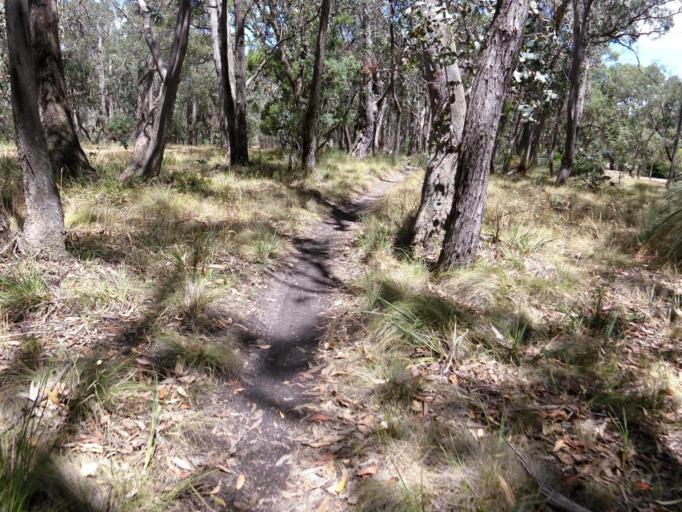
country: AU
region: Victoria
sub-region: Melton
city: Melton West
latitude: -37.4947
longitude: 144.5474
